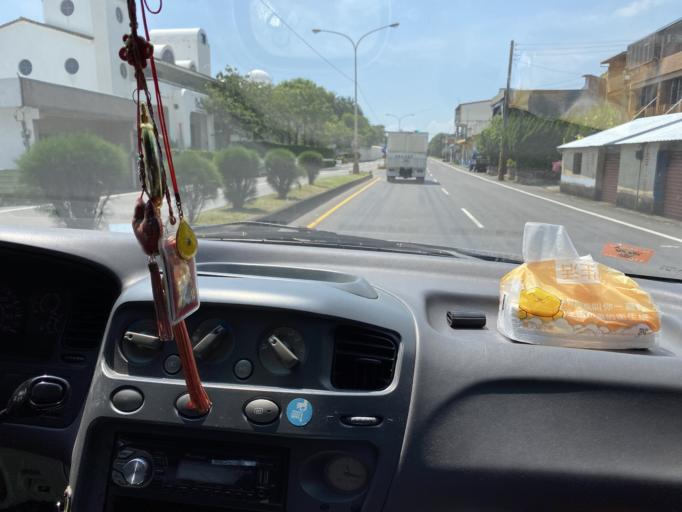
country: TW
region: Taiwan
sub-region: Yilan
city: Yilan
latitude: 24.8888
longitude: 121.8491
